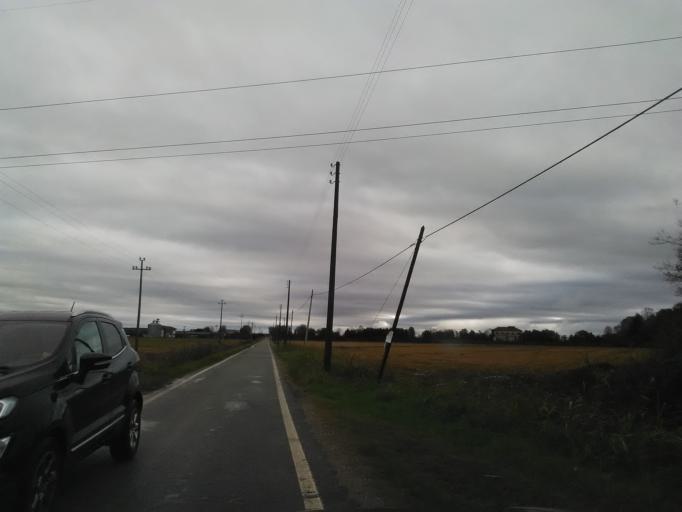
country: IT
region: Piedmont
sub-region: Provincia di Vercelli
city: Carisio
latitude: 45.4060
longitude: 8.2068
